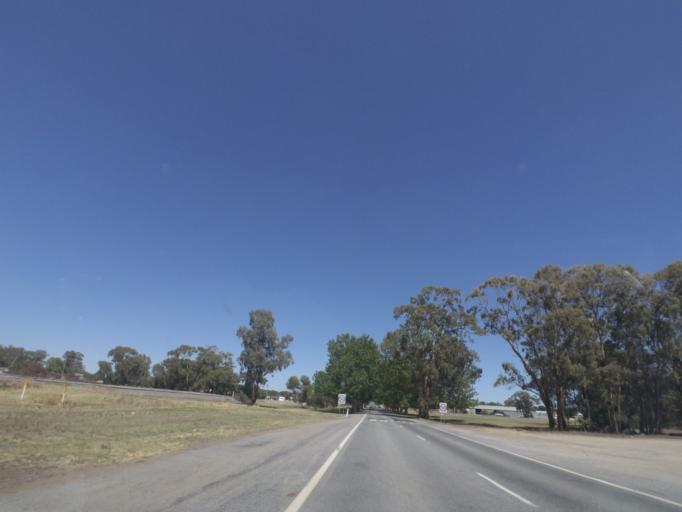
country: AU
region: New South Wales
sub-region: Narrandera
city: Narrandera
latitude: -34.7392
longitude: 146.5693
